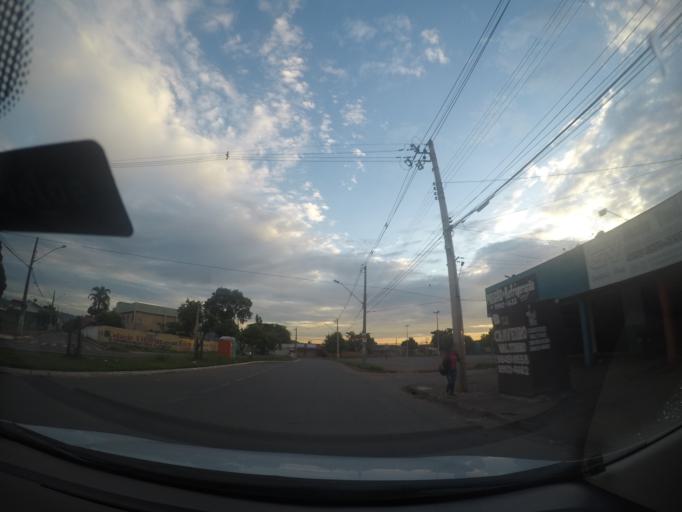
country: BR
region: Goias
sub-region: Goiania
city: Goiania
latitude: -16.6967
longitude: -49.3508
